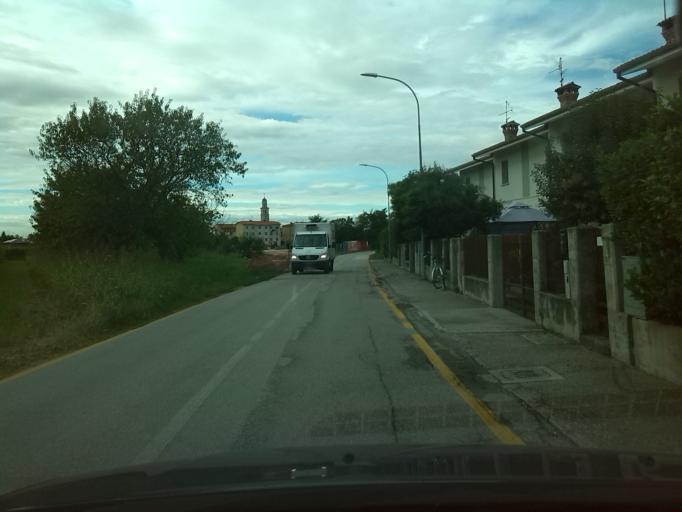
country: IT
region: Friuli Venezia Giulia
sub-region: Provincia di Gorizia
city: San Pier d'Isonzo
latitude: 45.8436
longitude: 13.4688
